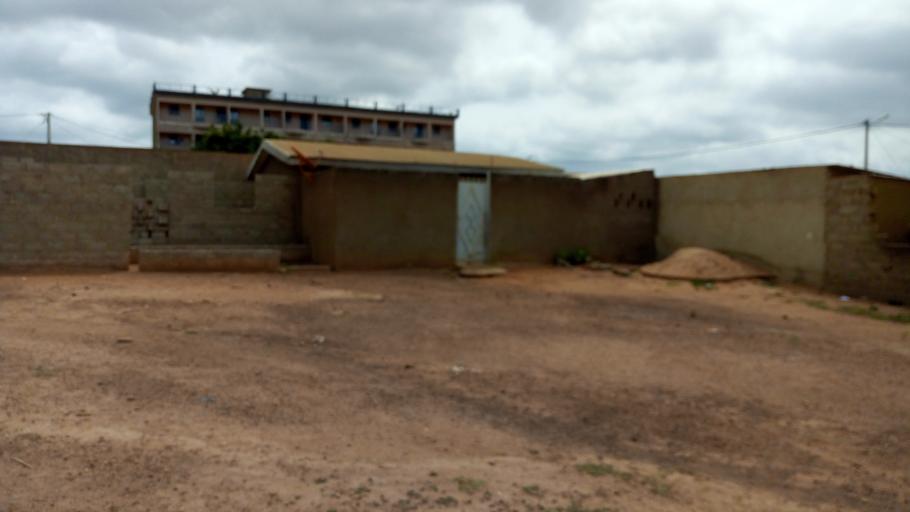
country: CI
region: Vallee du Bandama
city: Bouake
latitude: 7.7241
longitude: -5.0490
